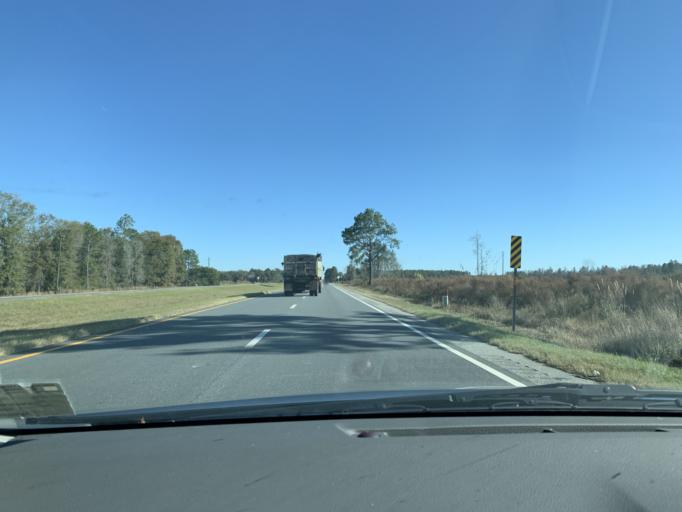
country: US
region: Georgia
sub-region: Atkinson County
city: Willacoochee
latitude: 31.3332
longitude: -83.0210
